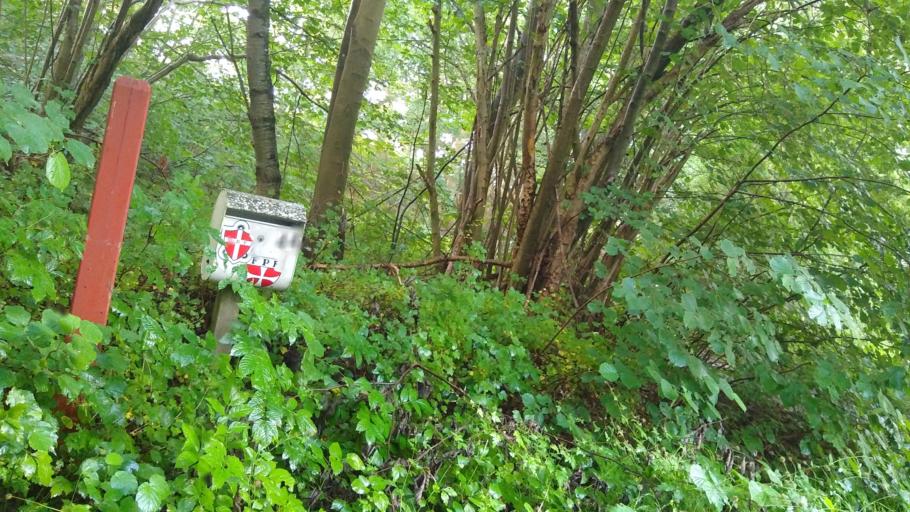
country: DK
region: South Denmark
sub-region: Fredericia Kommune
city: Fredericia
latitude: 55.6048
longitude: 9.7091
